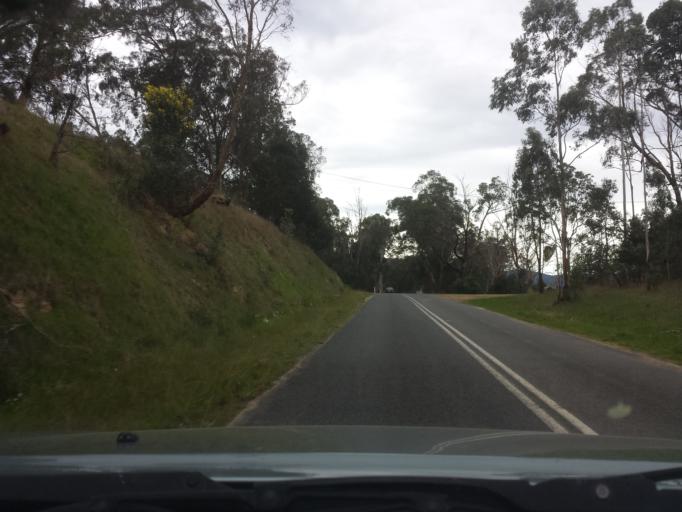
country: AU
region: Victoria
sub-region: Yarra Ranges
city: Yarra Glen
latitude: -37.6140
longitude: 145.3708
